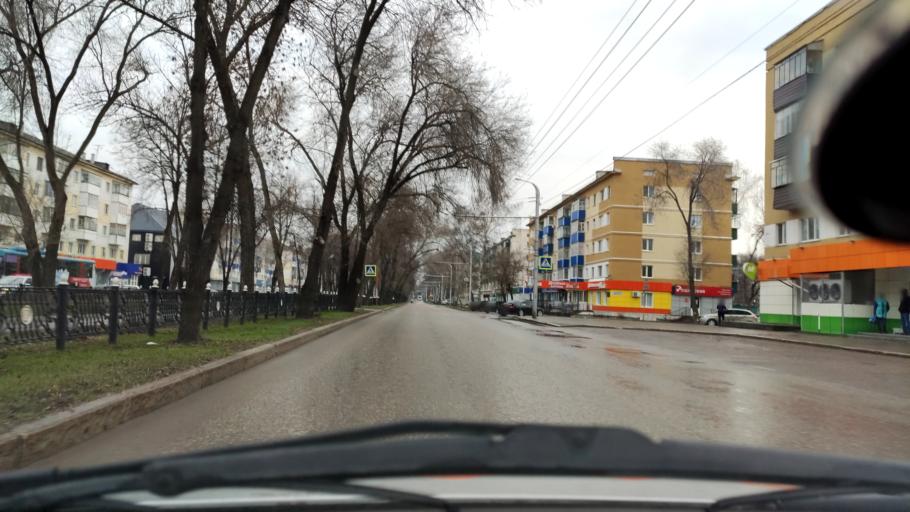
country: RU
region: Bashkortostan
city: Sterlitamak
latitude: 53.6393
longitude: 55.9387
